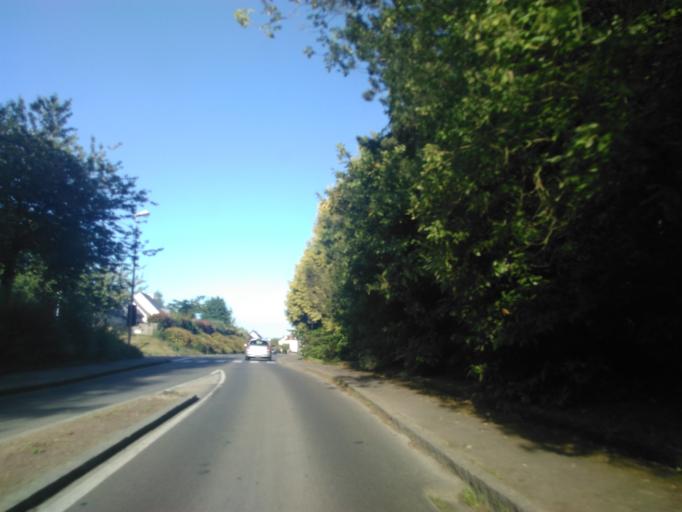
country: FR
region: Brittany
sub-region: Departement d'Ille-et-Vilaine
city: Geveze
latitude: 48.2214
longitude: -1.7971
